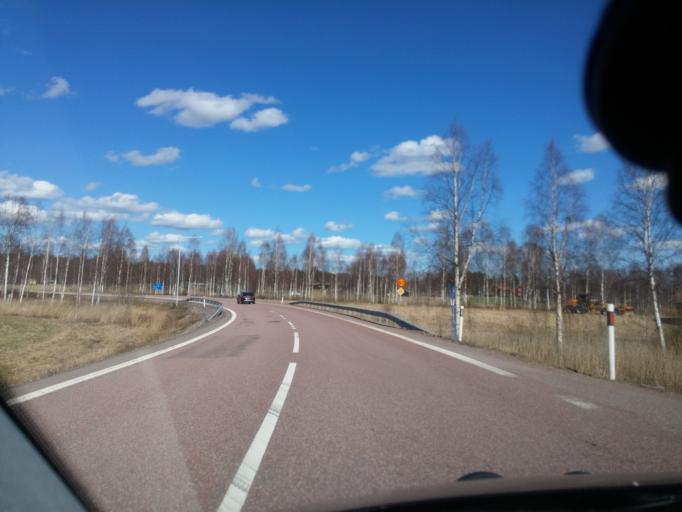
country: SE
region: Dalarna
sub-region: Faluns Kommun
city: Svardsjo
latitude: 60.7137
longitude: 15.7807
